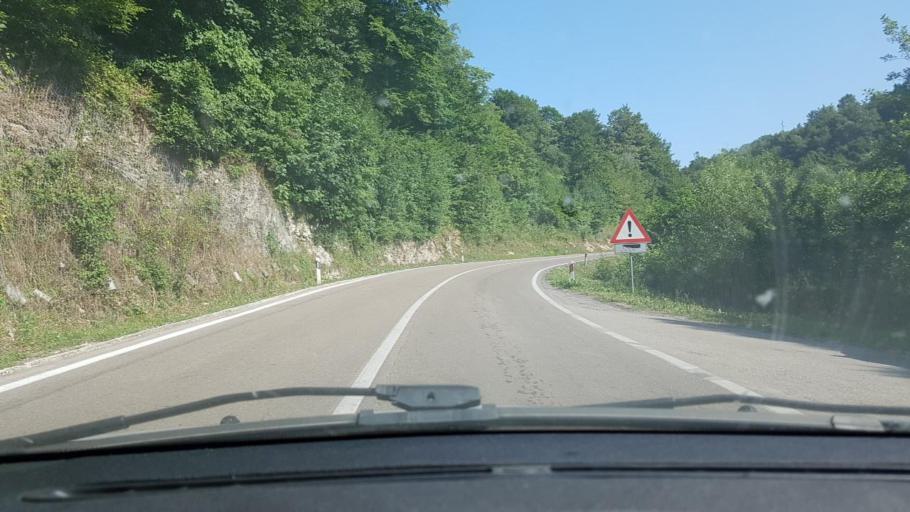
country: BA
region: Federation of Bosnia and Herzegovina
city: Skokovi
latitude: 45.0016
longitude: 15.9066
